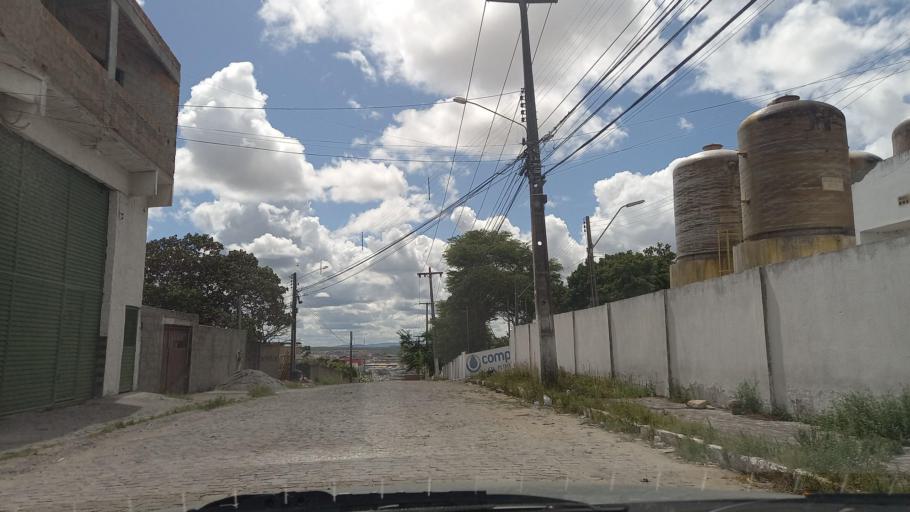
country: BR
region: Pernambuco
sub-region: Caruaru
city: Caruaru
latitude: -8.3012
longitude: -35.9797
